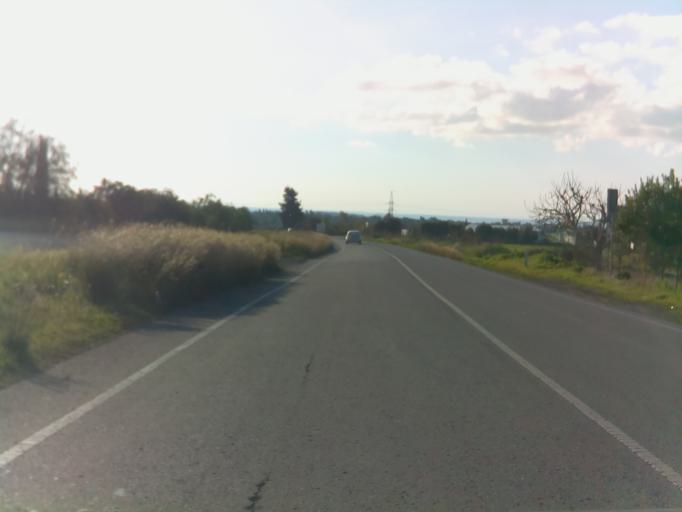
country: CY
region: Pafos
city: Paphos
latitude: 34.7453
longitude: 32.4740
